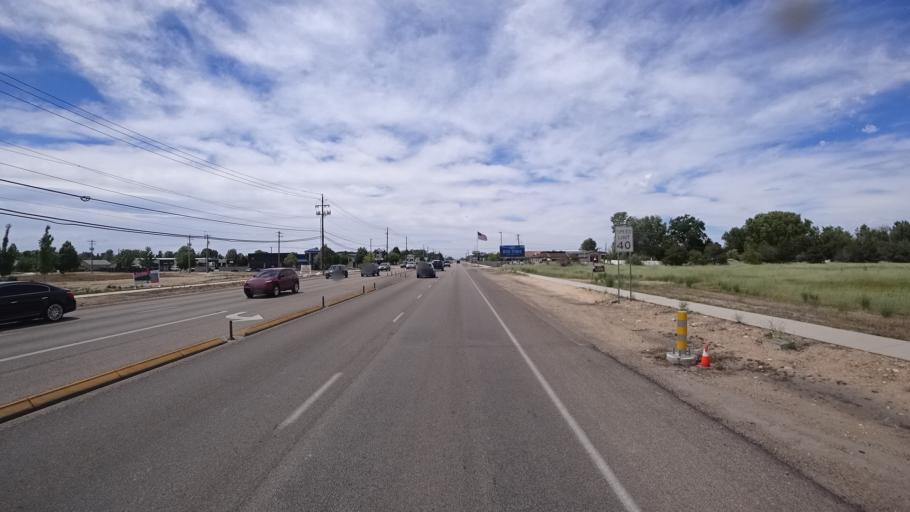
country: US
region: Idaho
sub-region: Ada County
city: Meridian
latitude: 43.6195
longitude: -116.3231
